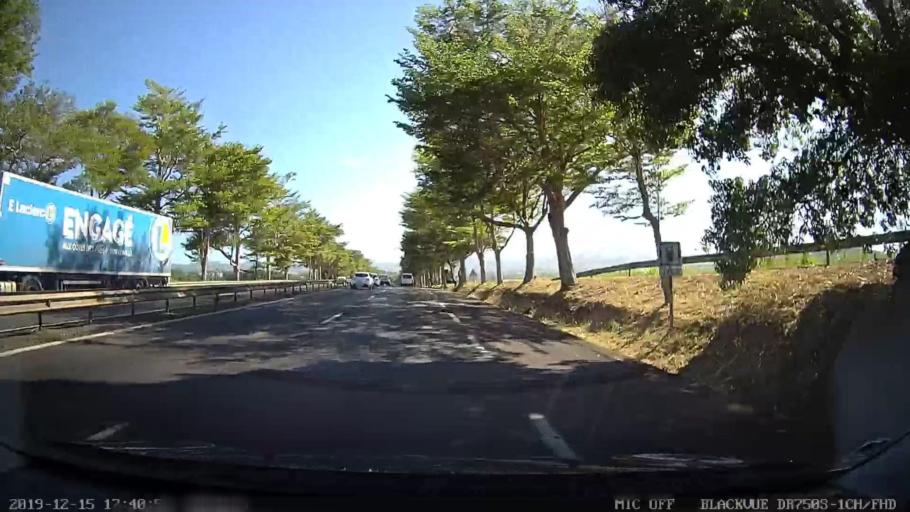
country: RE
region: Reunion
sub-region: Reunion
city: Saint-Pierre
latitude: -21.3147
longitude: 55.4932
